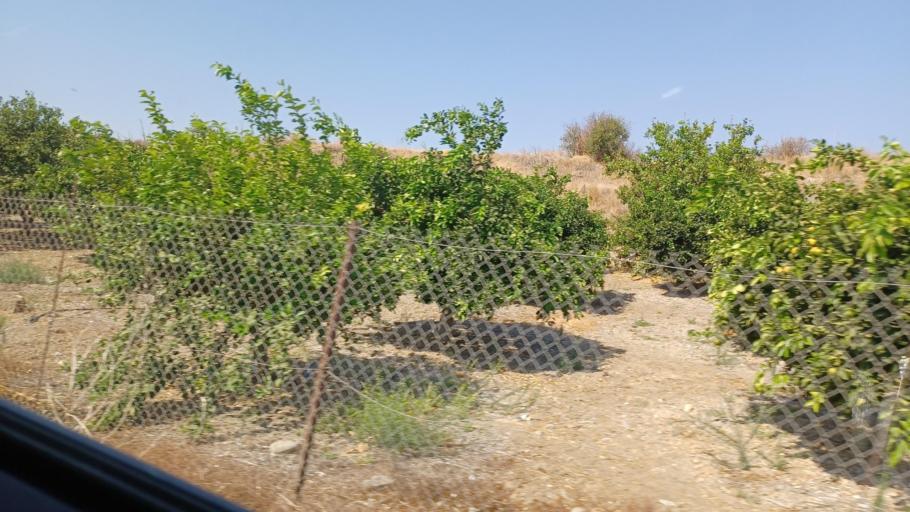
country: CY
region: Pafos
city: Polis
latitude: 35.0460
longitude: 32.4452
